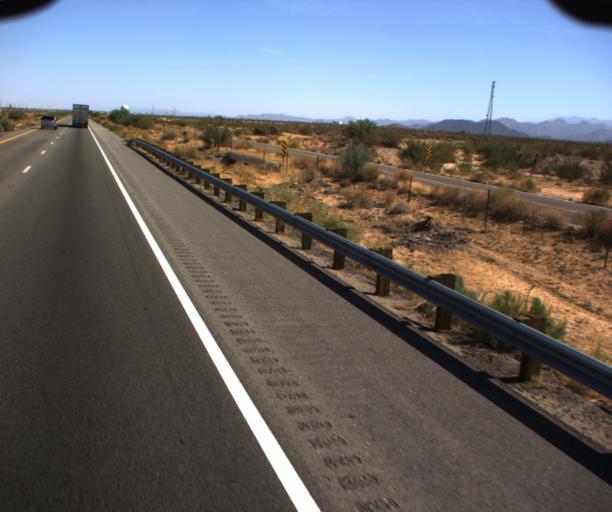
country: US
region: Arizona
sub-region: Mohave County
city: Kingman
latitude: 34.8511
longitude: -114.1460
